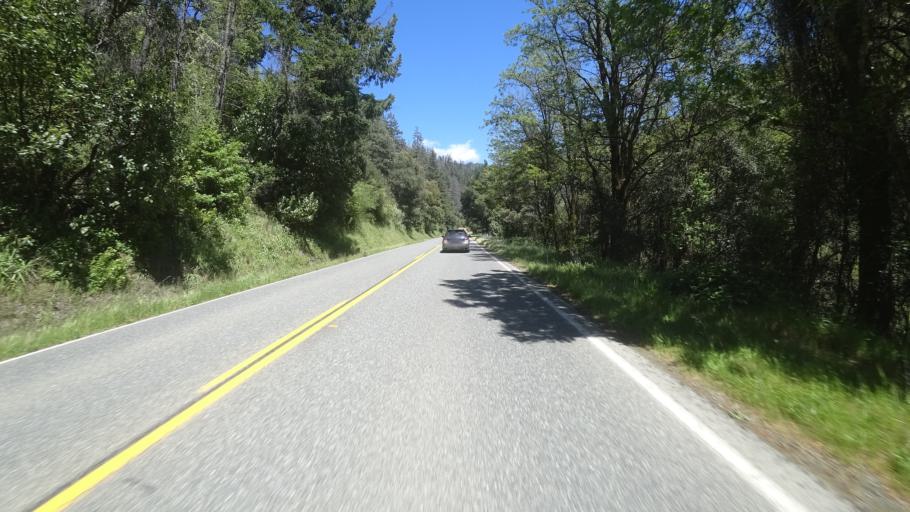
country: US
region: California
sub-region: Trinity County
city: Hayfork
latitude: 40.7760
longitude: -123.3244
